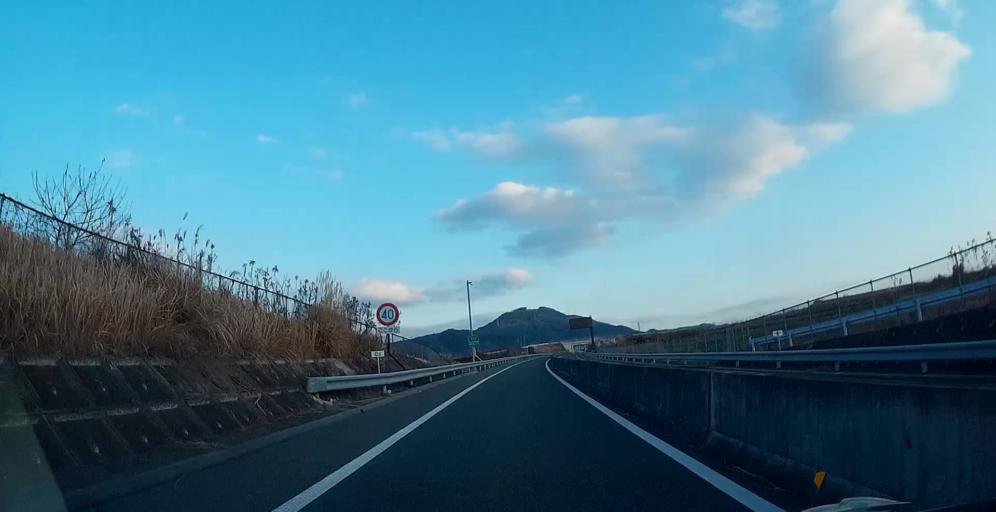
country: JP
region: Kumamoto
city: Kumamoto
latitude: 32.7533
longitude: 130.7941
